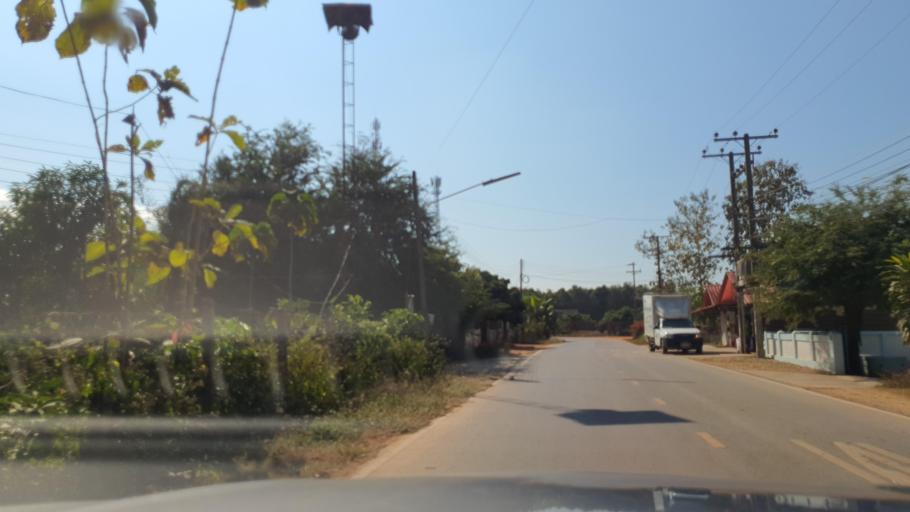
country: TH
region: Nan
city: Pua
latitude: 19.1425
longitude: 100.9242
